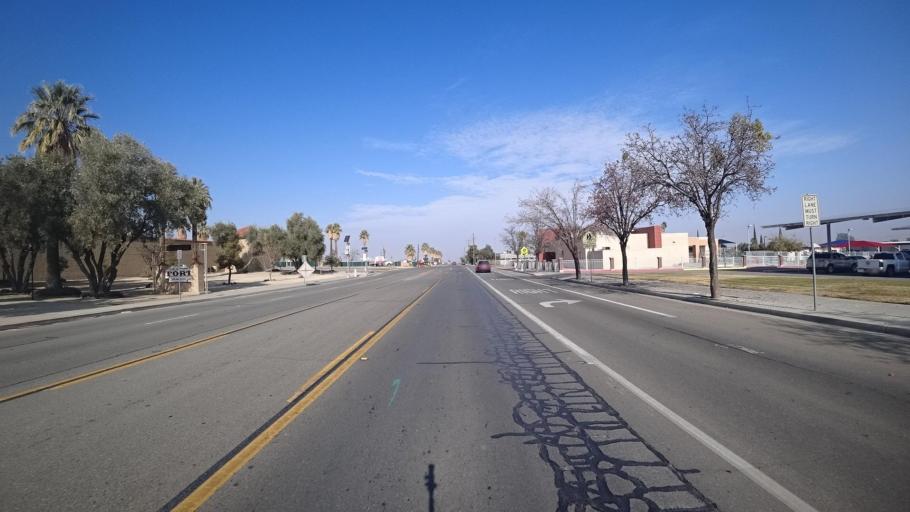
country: US
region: California
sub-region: Kern County
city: Ford City
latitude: 35.1502
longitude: -119.4651
